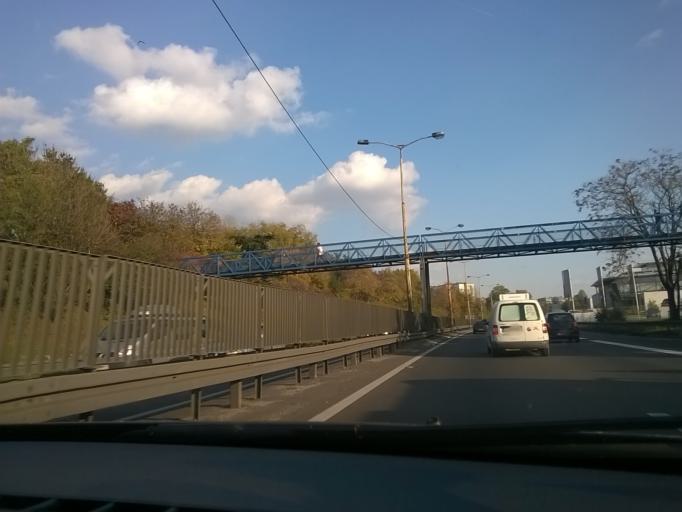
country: RS
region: Central Serbia
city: Belgrade
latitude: 44.7952
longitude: 20.4589
